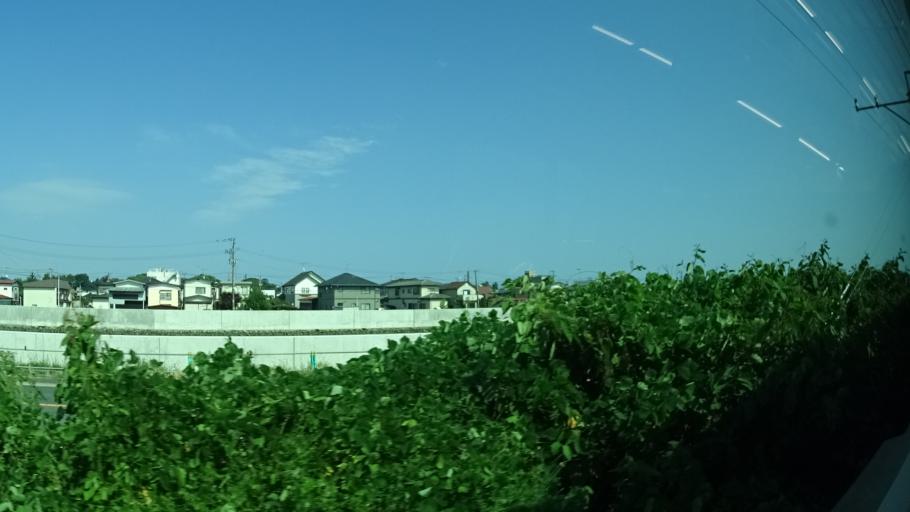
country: JP
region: Miyagi
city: Matsushima
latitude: 38.3852
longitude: 141.0675
